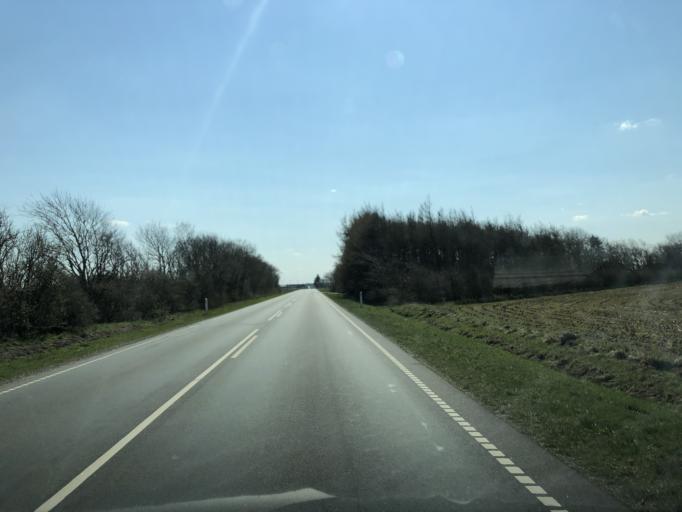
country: DK
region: Central Jutland
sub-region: Lemvig Kommune
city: Lemvig
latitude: 56.4494
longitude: 8.2946
